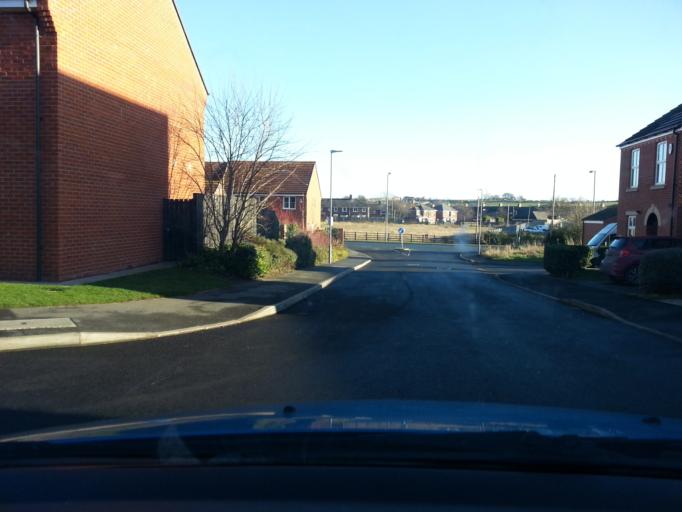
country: GB
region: England
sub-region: County Durham
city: Crook
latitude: 54.7099
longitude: -1.7531
